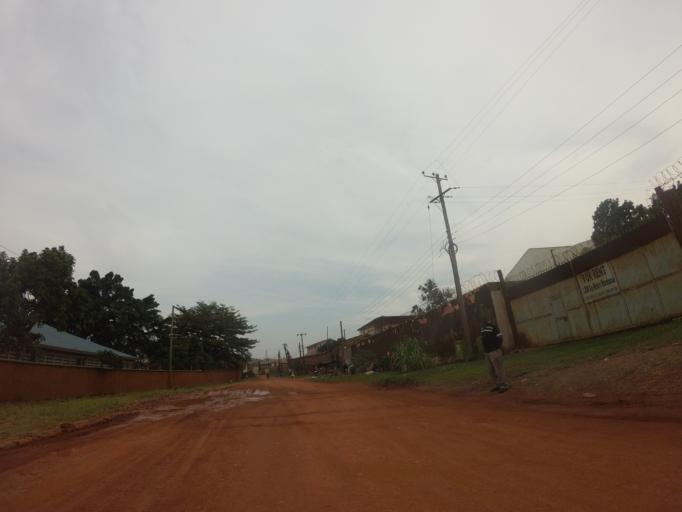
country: UG
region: Central Region
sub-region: Wakiso District
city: Kireka
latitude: 0.3414
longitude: 32.6226
